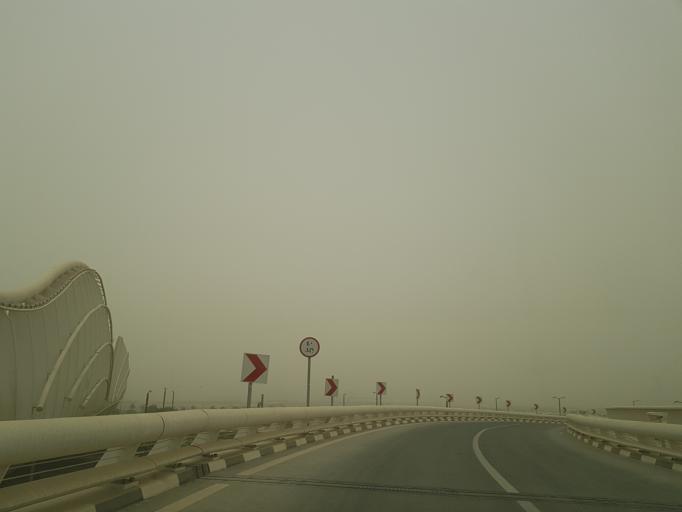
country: AE
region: Dubai
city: Dubai
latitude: 25.1604
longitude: 55.2973
